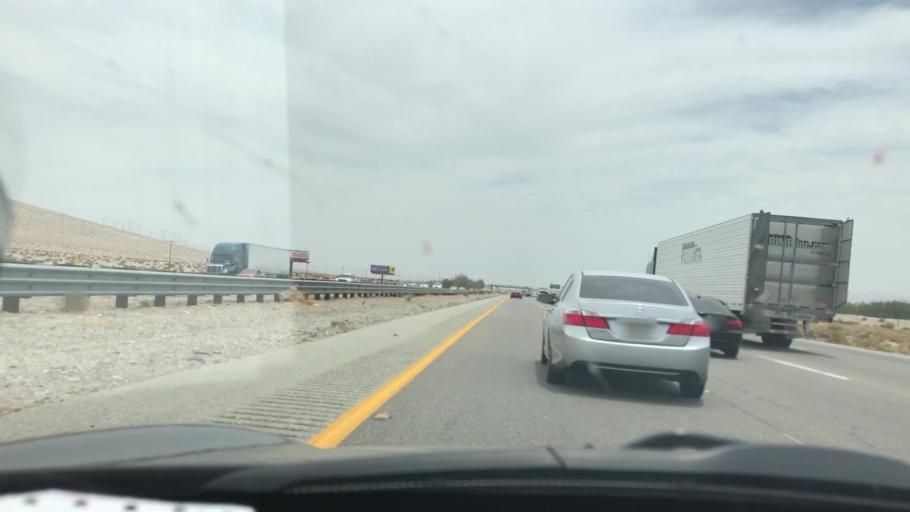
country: US
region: California
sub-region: Riverside County
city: Desert Edge
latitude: 33.8579
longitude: -116.4730
